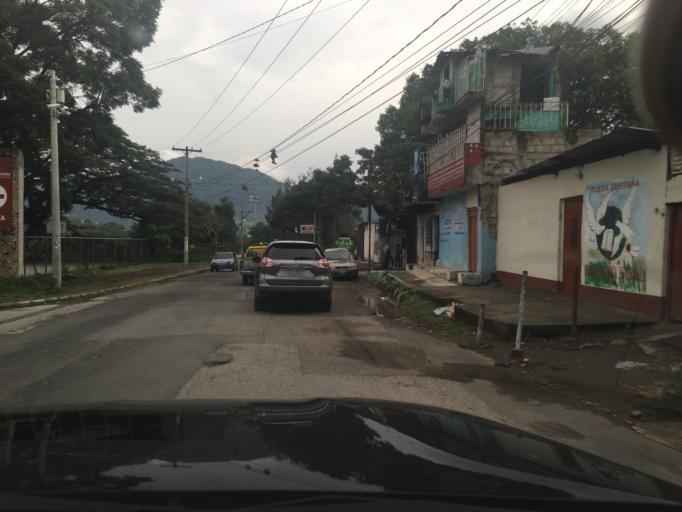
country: GT
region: Guatemala
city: Amatitlan
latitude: 14.4897
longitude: -90.6169
